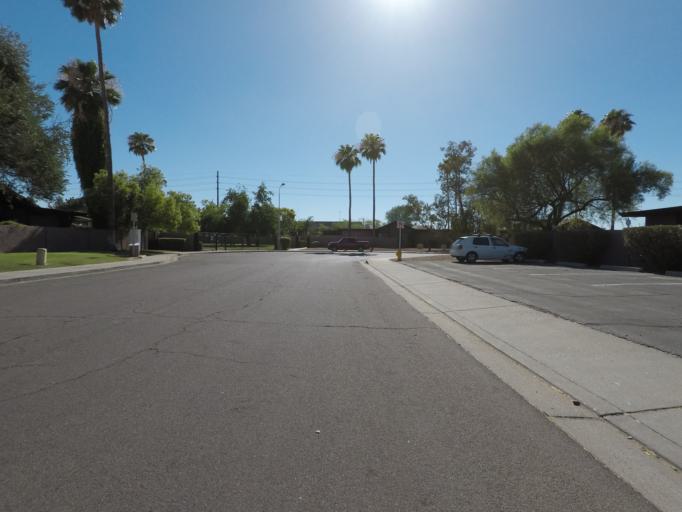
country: US
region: Arizona
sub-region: Maricopa County
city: Tempe
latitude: 33.4201
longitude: -111.9080
